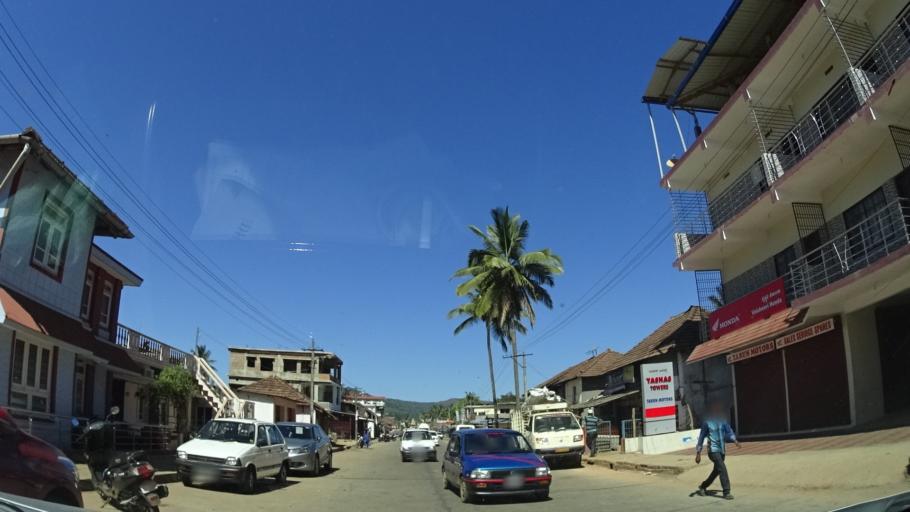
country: IN
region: Karnataka
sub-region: Chikmagalur
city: Sringeri
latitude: 13.2329
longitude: 75.3620
